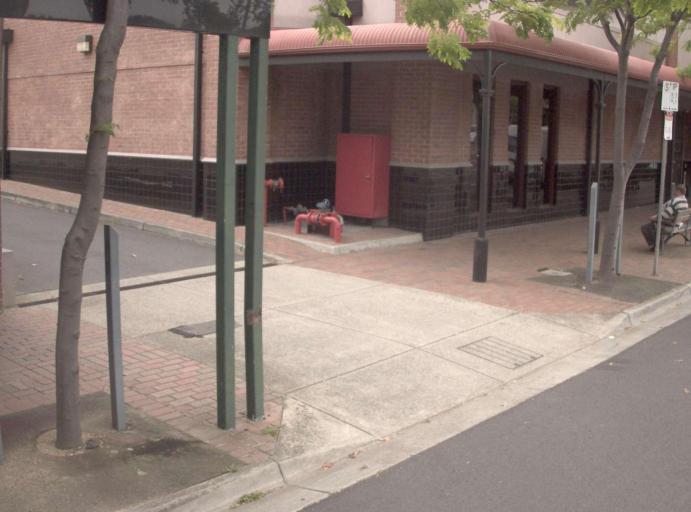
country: AU
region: Victoria
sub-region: Casey
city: Cranbourne
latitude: -38.1112
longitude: 145.2833
